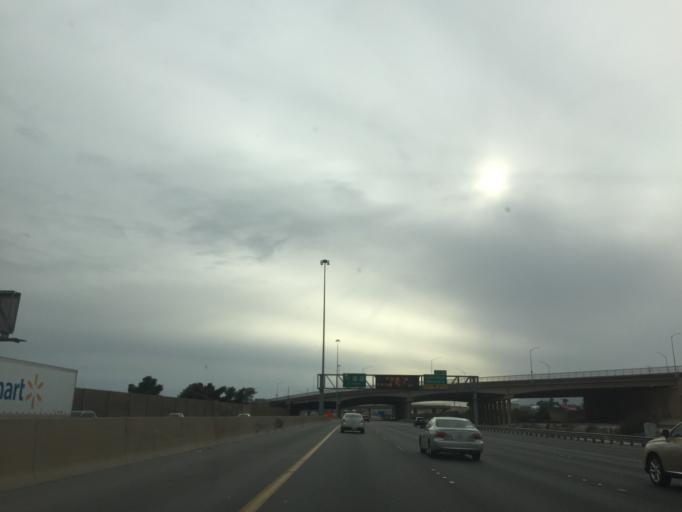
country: US
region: Nevada
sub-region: Clark County
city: North Las Vegas
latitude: 36.2076
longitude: -115.1317
